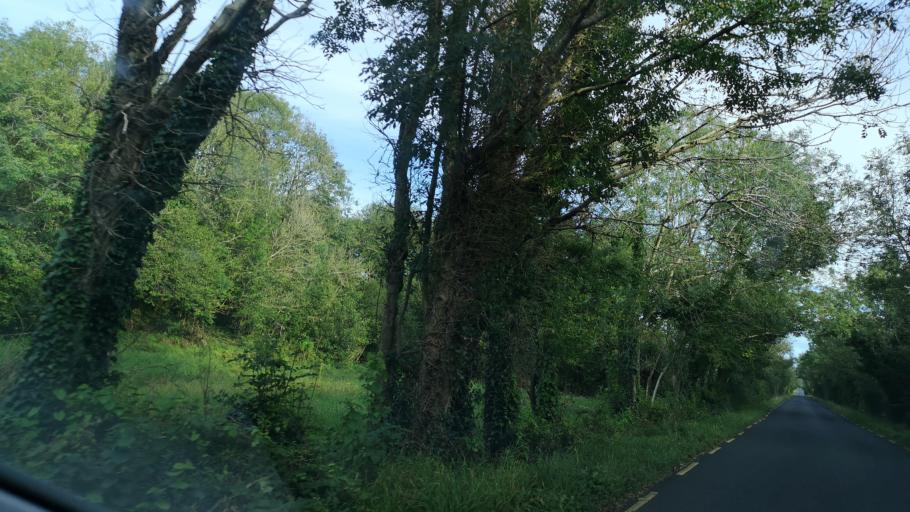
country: IE
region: Connaught
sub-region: County Galway
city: Ballinasloe
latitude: 53.3369
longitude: -8.2878
